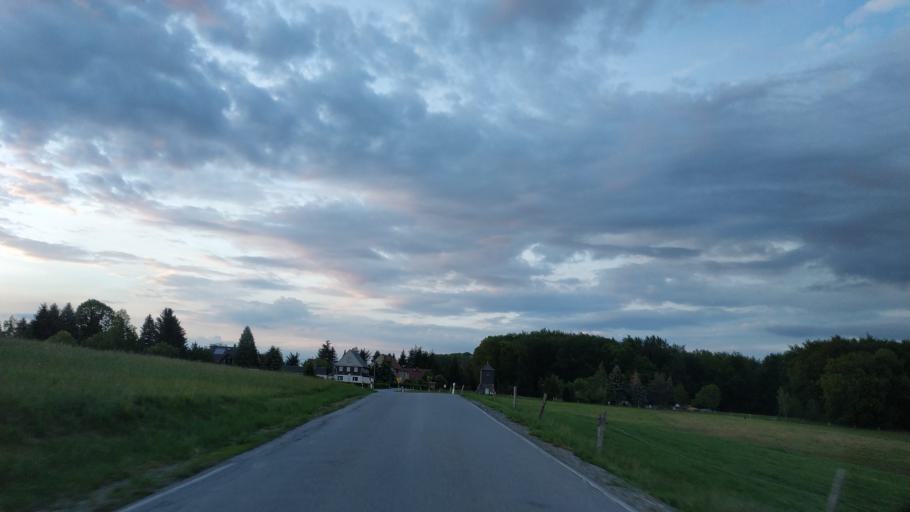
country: DE
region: Saxony
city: Lohmen
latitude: 50.9834
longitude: 14.0242
